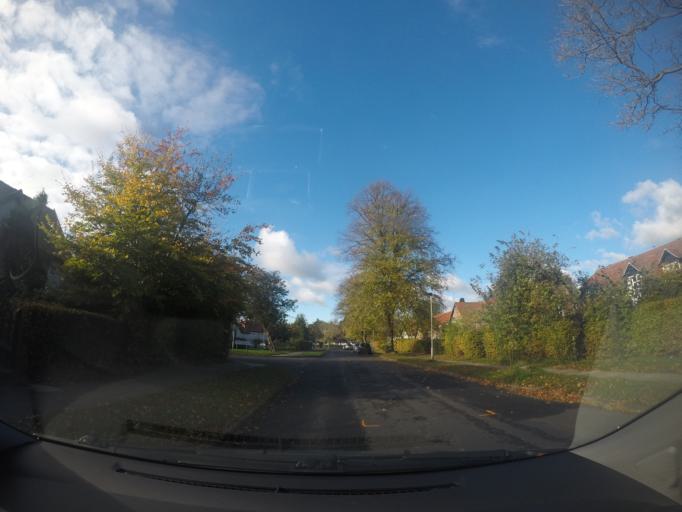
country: GB
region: England
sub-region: City of York
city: Huntington
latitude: 53.9892
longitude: -1.0714
